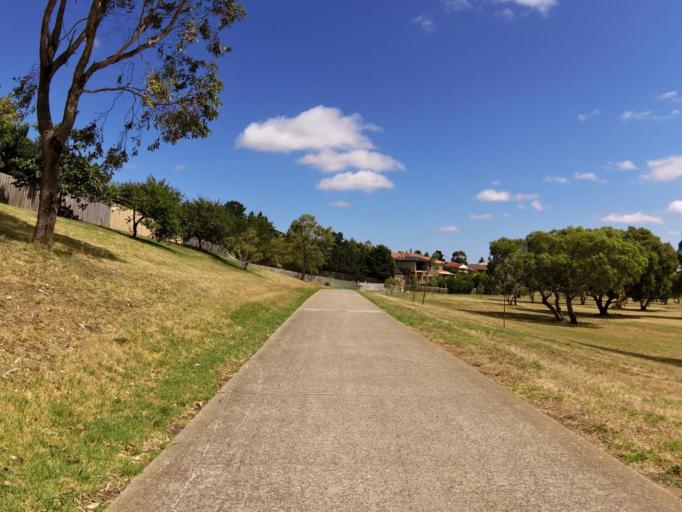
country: AU
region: Victoria
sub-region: Hume
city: Meadow Heights
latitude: -37.6430
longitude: 144.9216
